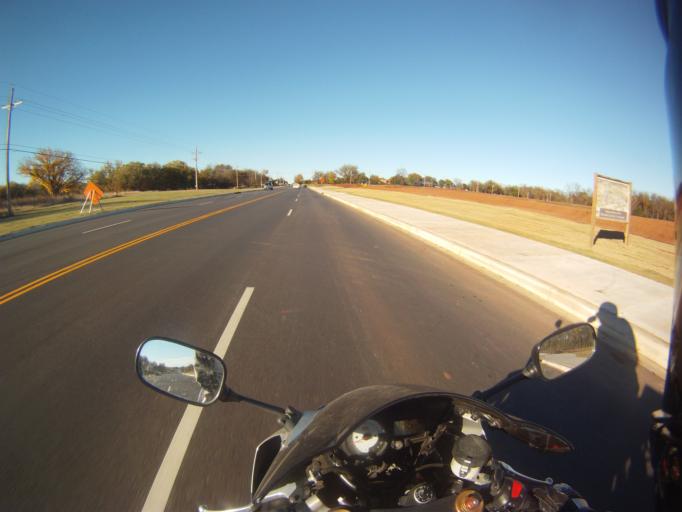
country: US
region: Oklahoma
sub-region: Payne County
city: Stillwater
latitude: 36.1280
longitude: -97.1230
